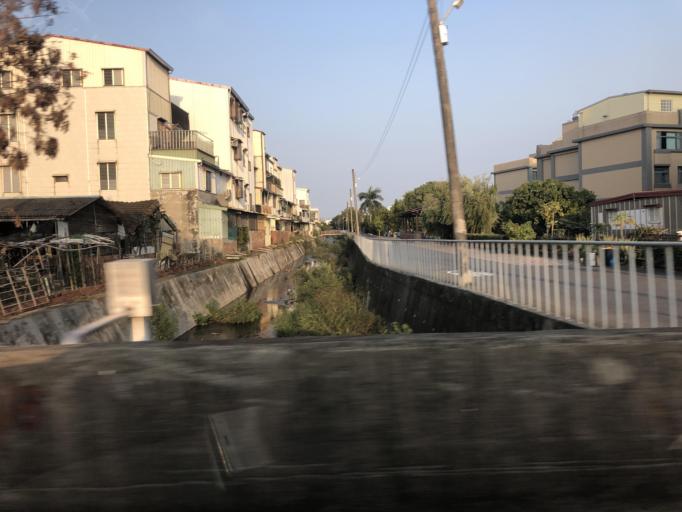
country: TW
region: Taiwan
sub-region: Tainan
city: Tainan
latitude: 23.1258
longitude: 120.2507
